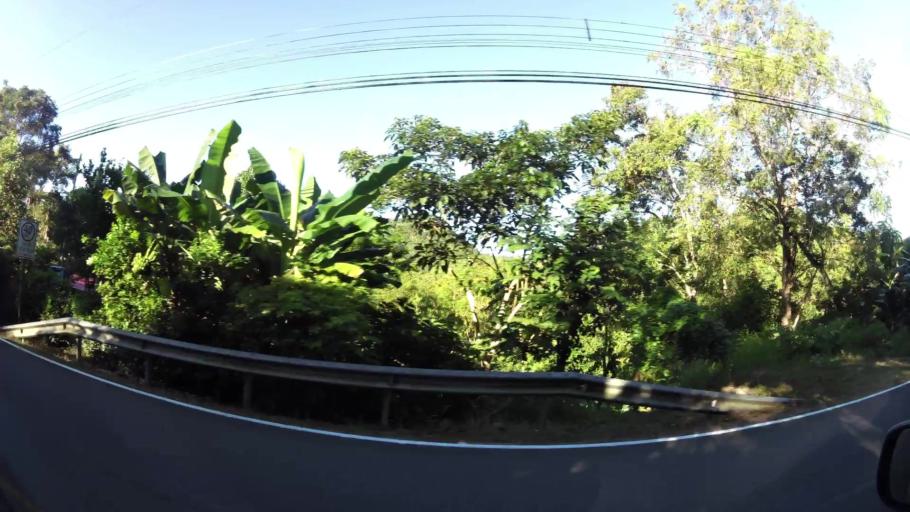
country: CR
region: Guanacaste
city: Juntas
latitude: 10.1973
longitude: -84.8434
